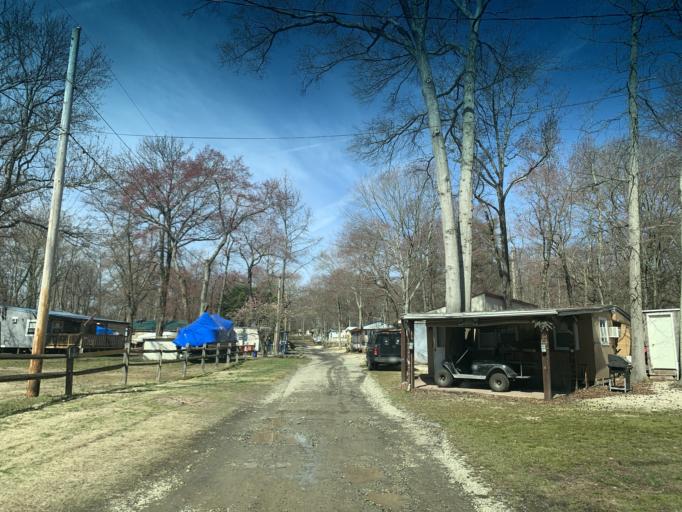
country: US
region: Maryland
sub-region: Cecil County
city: Charlestown
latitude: 39.5515
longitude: -76.0081
